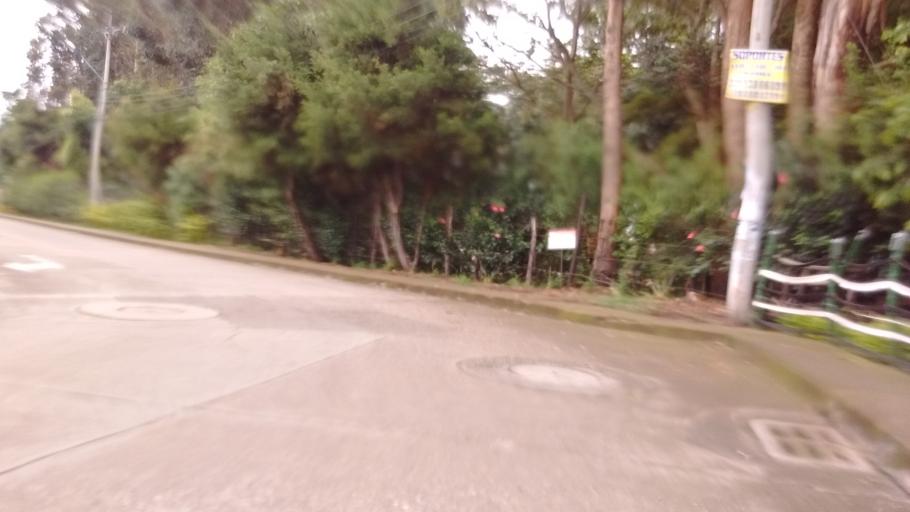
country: CO
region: Cauca
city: Popayan
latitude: 2.4812
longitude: -76.5773
